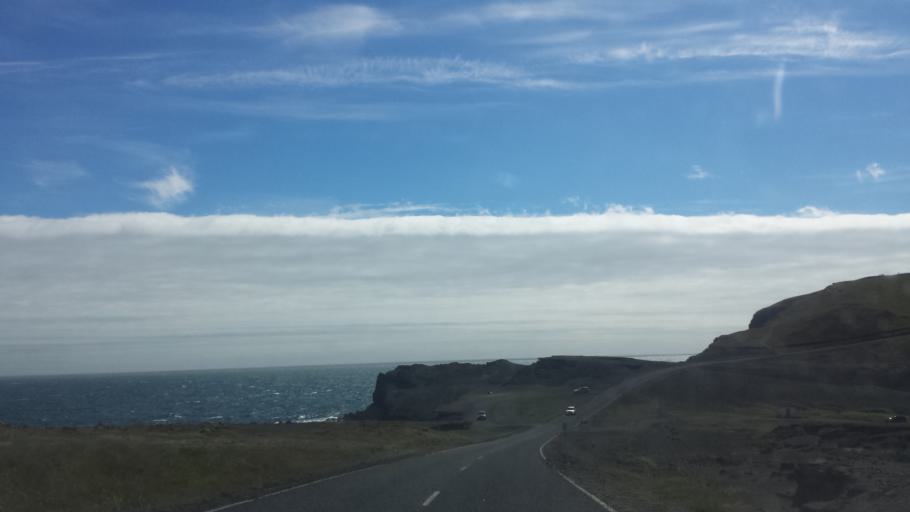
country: IS
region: South
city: Vestmannaeyjar
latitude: 63.4077
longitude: -20.2763
